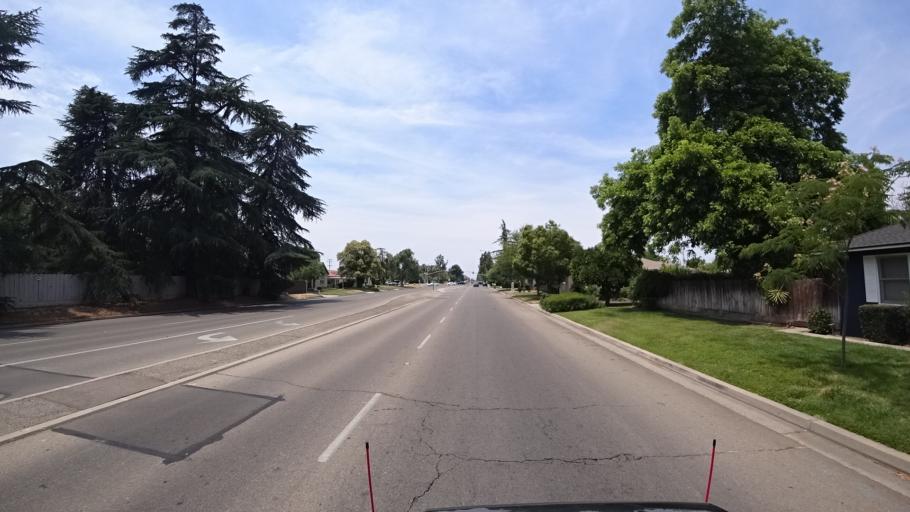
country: US
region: California
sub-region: Fresno County
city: Sunnyside
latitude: 36.7505
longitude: -119.7163
